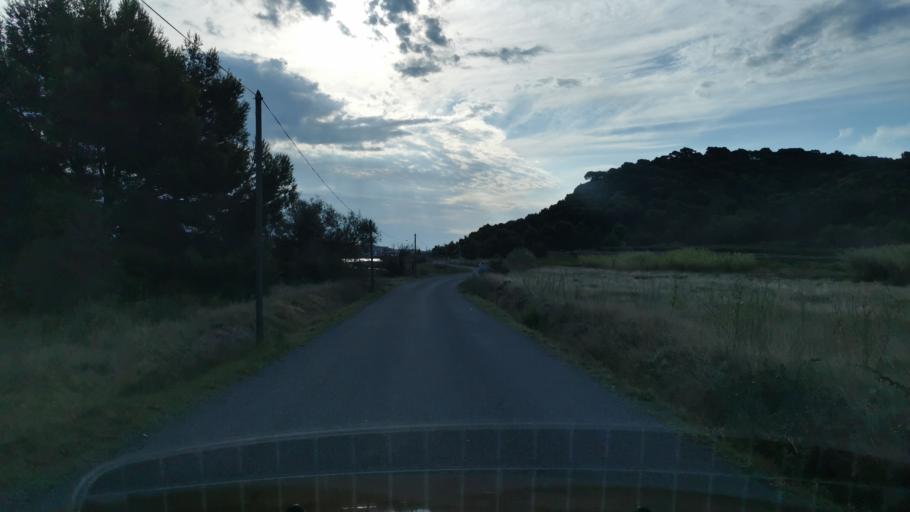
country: FR
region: Languedoc-Roussillon
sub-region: Departement de l'Aude
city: Gruissan
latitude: 43.1074
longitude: 3.0740
